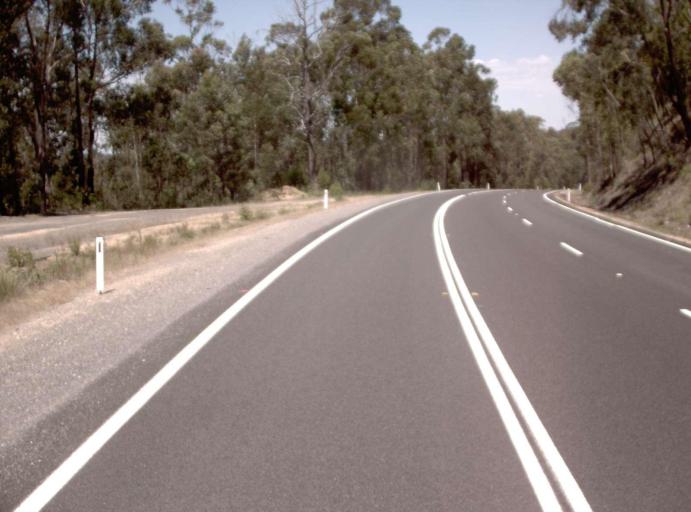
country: AU
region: Victoria
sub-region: East Gippsland
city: Lakes Entrance
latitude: -37.7063
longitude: 148.6513
